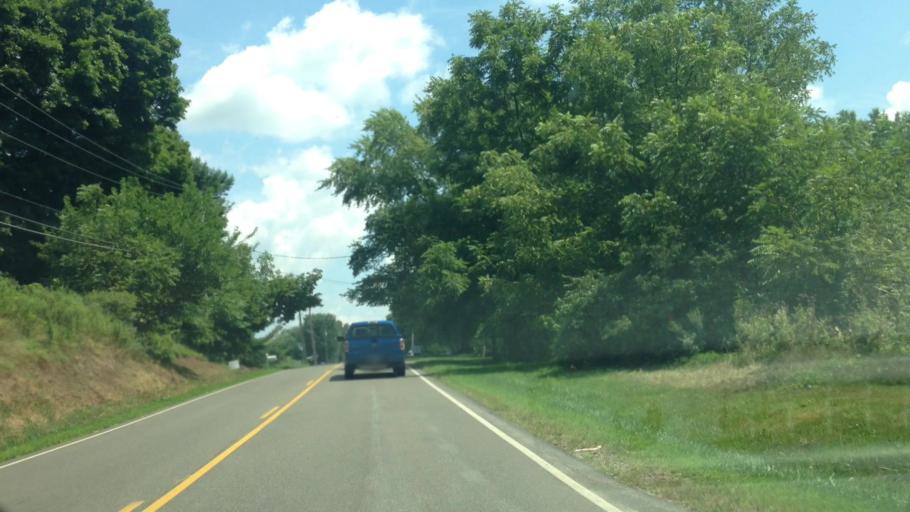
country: US
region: Ohio
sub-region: Summit County
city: New Franklin
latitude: 40.9494
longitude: -81.5404
